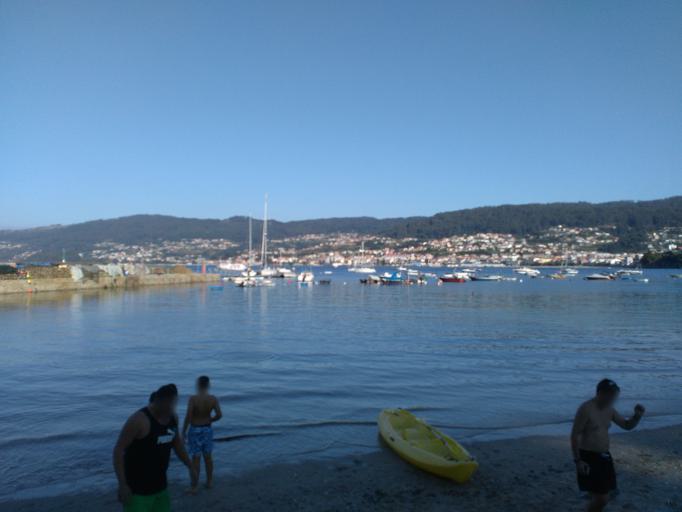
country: ES
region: Galicia
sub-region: Provincia de Pontevedra
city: Bueu
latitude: 42.3332
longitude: -8.8007
